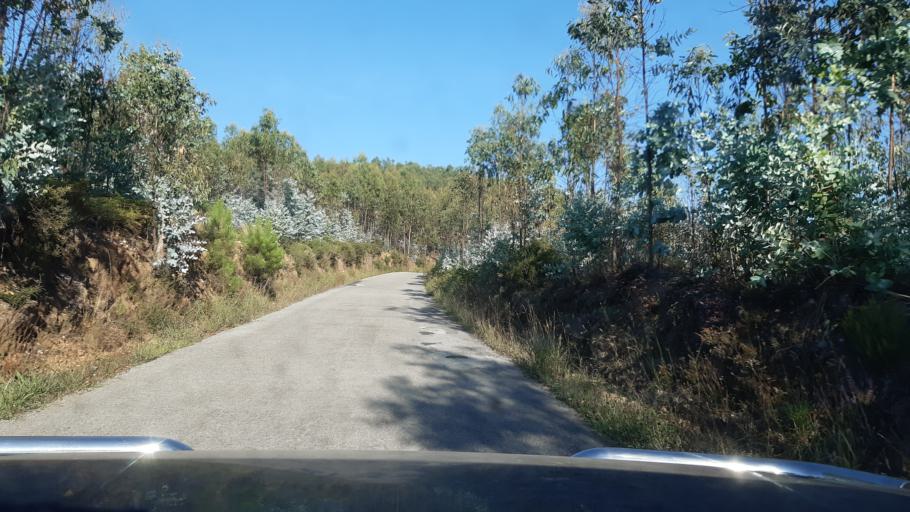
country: PT
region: Aveiro
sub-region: Agueda
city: Aguada de Cima
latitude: 40.5678
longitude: -8.3229
